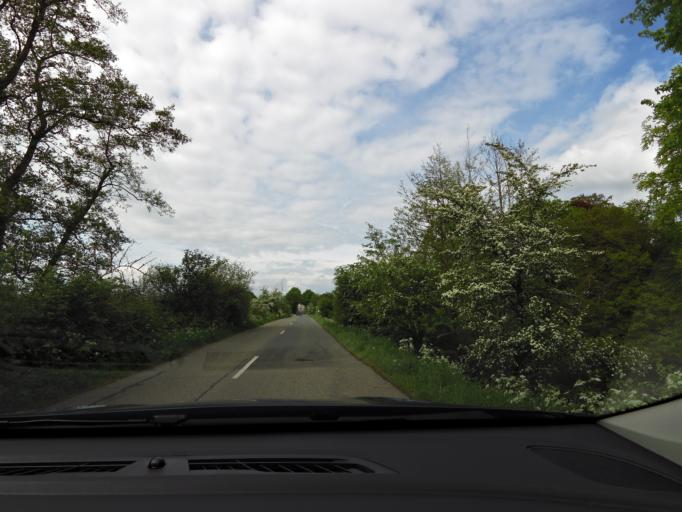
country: NL
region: Utrecht
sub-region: Gemeente Utrechtse Heuvelrug
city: Amerongen
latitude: 51.9945
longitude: 5.4569
